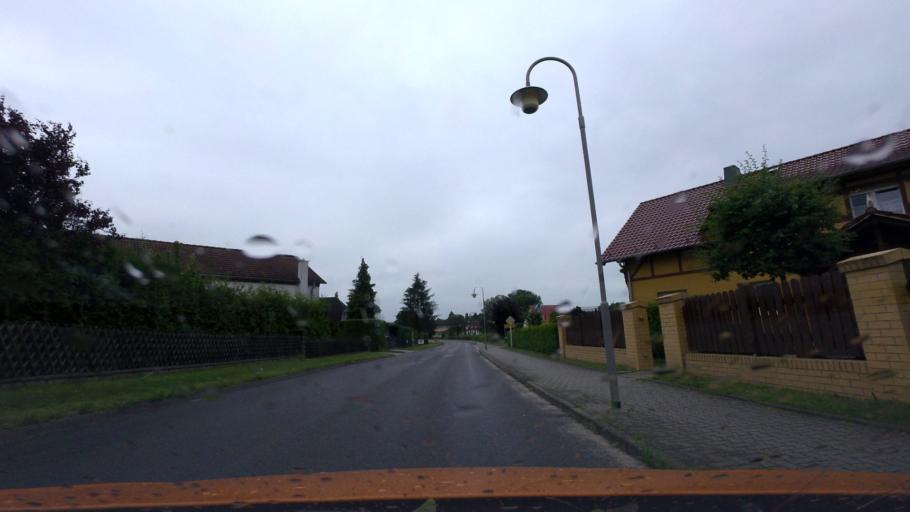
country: DE
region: Brandenburg
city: Strausberg
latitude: 52.6077
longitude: 13.8701
